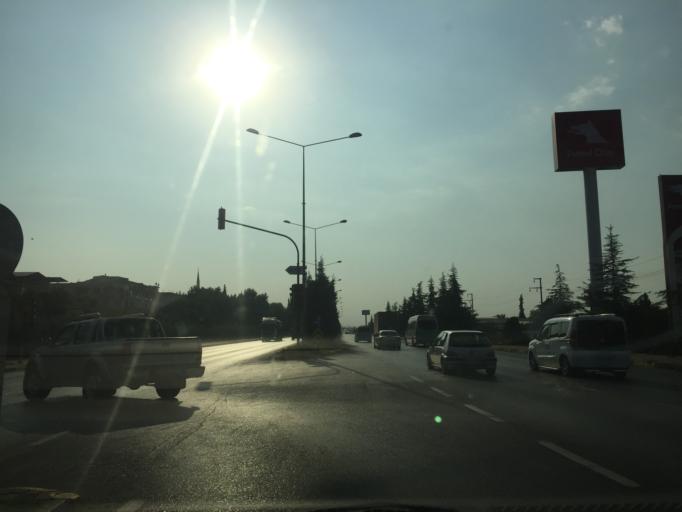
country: TR
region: Manisa
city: Salihli
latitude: 38.4895
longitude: 28.1515
